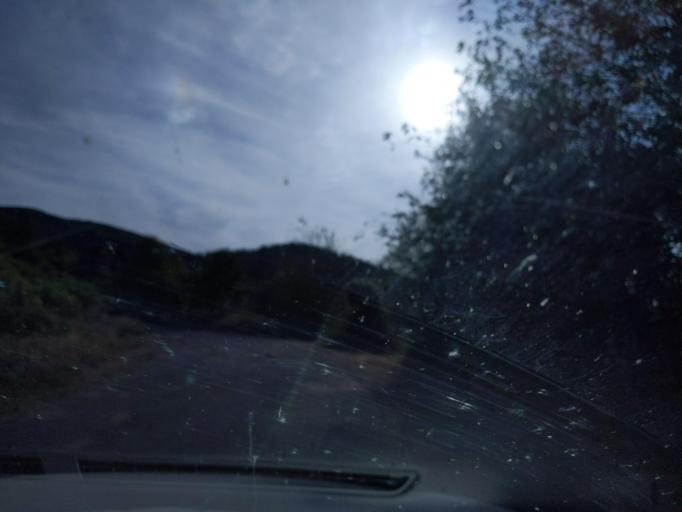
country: ES
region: La Rioja
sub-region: Provincia de La Rioja
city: Ezcaray
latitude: 42.3220
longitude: -3.0224
